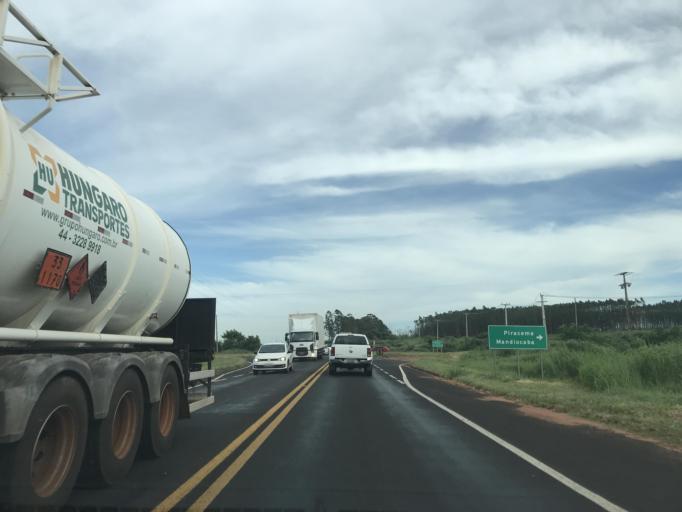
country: BR
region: Parana
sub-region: Paranavai
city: Nova Aurora
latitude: -22.9916
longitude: -52.5935
